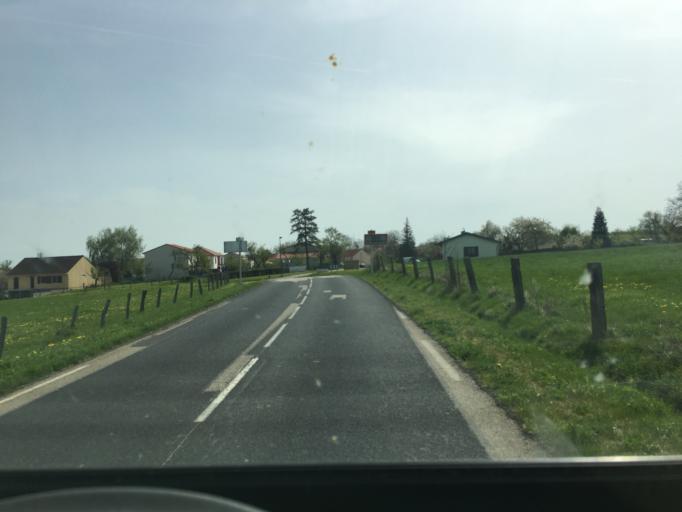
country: FR
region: Lorraine
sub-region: Departement de Meurthe-et-Moselle
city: Fleville-devant-Nancy
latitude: 48.6126
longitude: 6.2486
